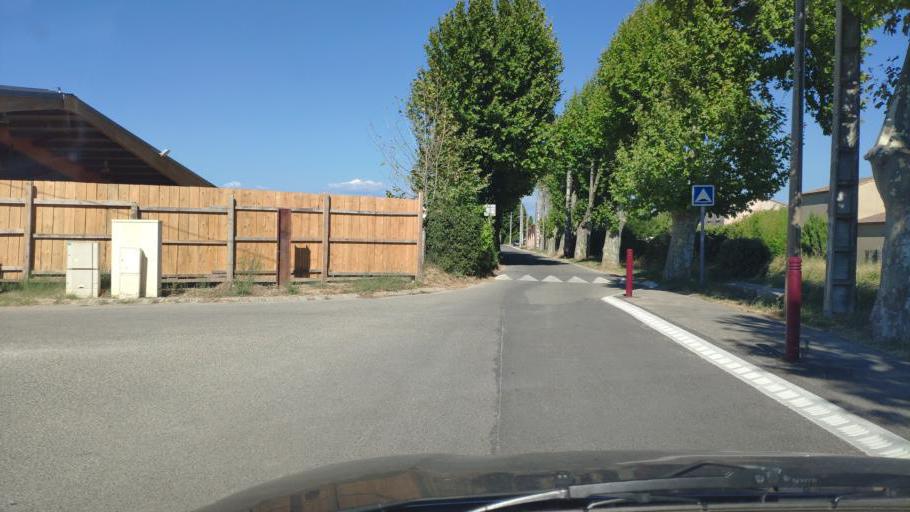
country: FR
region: Provence-Alpes-Cote d'Azur
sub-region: Departement du Vaucluse
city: Entraigues-sur-la-Sorgue
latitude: 43.9995
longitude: 4.9125
